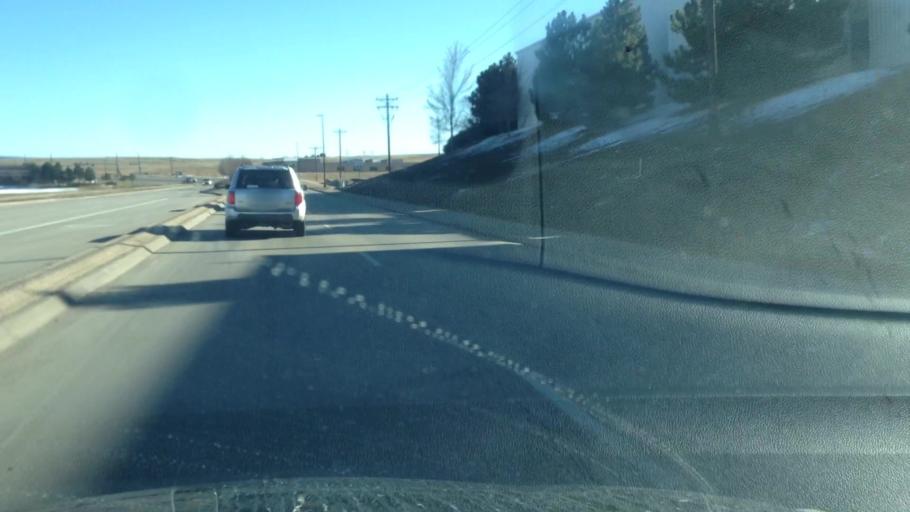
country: US
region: Colorado
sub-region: Arapahoe County
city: Dove Valley
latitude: 39.5858
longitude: -104.8158
